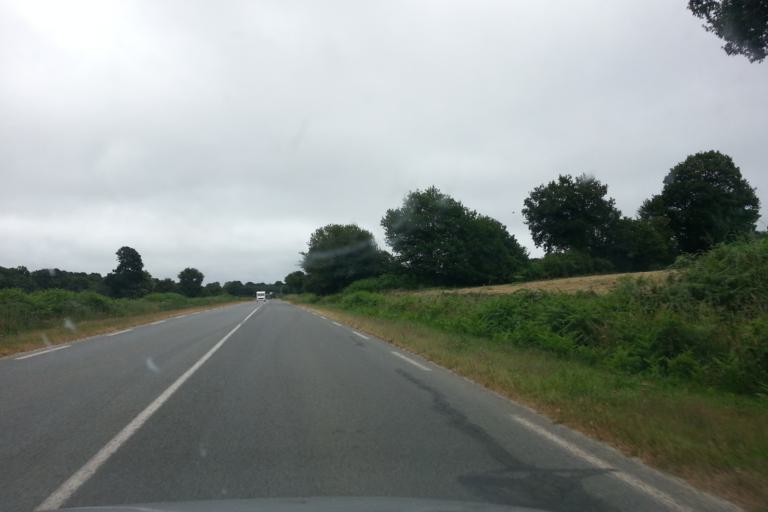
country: FR
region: Brittany
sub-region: Departement des Cotes-d'Armor
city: Gouarec
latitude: 48.2138
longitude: -3.1182
